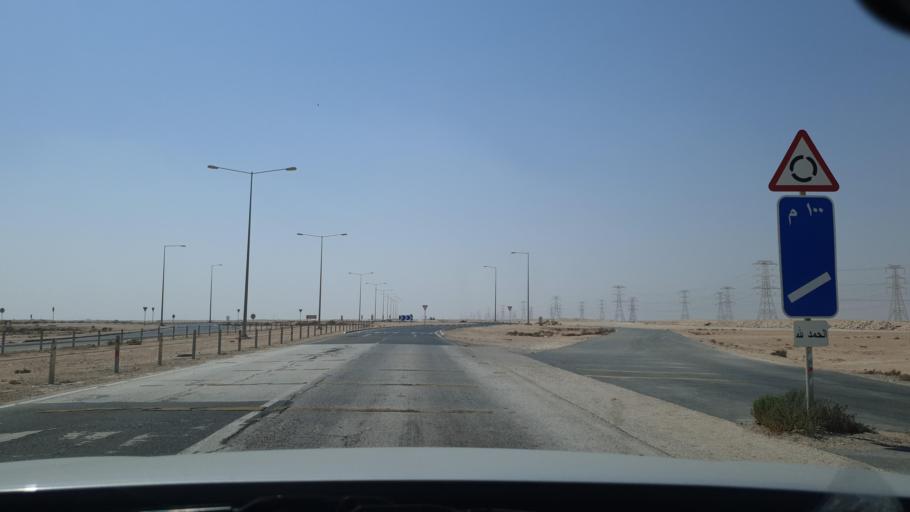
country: QA
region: Al Khawr
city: Al Khawr
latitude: 25.7330
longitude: 51.4577
